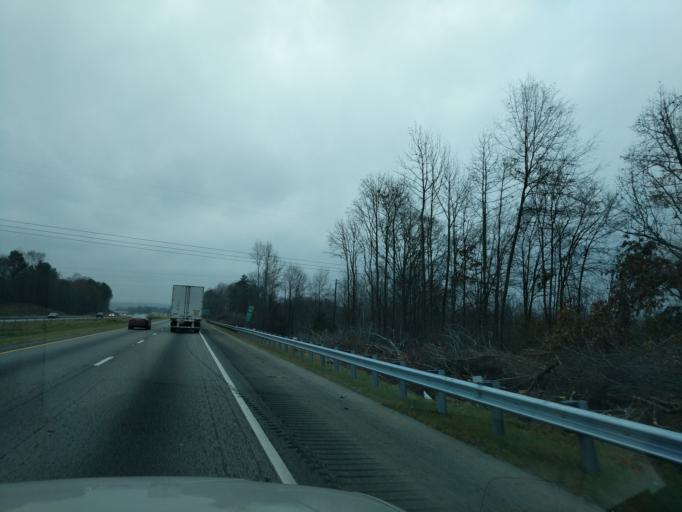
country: US
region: Georgia
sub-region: Jackson County
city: Jefferson
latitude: 34.1613
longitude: -83.6331
